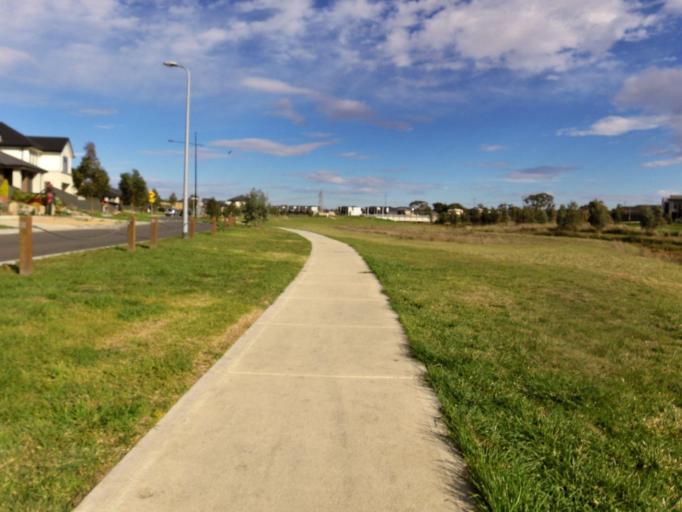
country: AU
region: Victoria
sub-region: Whittlesea
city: Epping
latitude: -37.6208
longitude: 145.0412
